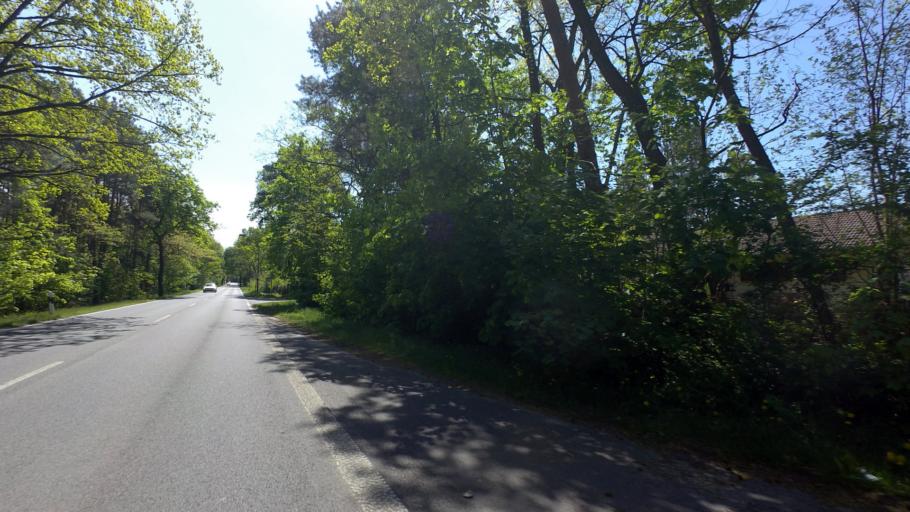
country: DE
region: Brandenburg
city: Bestensee
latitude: 52.2481
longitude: 13.6586
